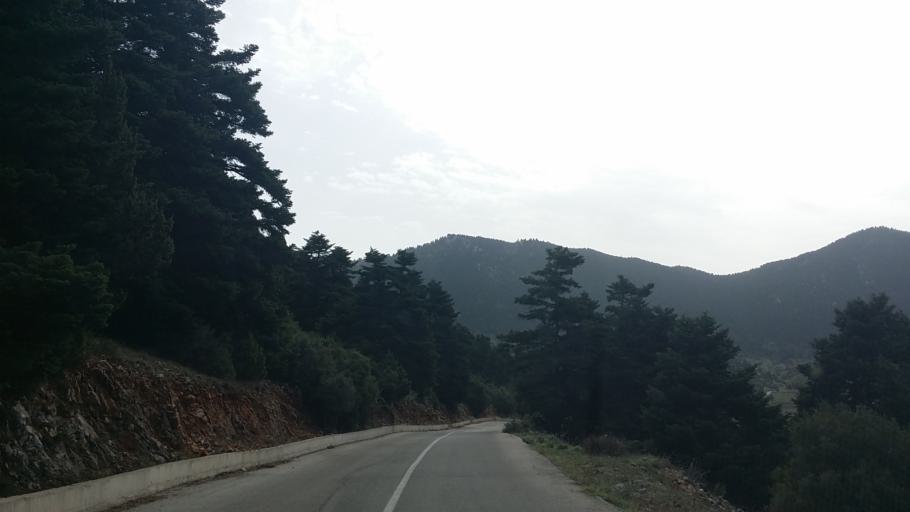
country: GR
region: Central Greece
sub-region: Nomos Voiotias
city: Livadeia
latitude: 38.3815
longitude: 22.8393
